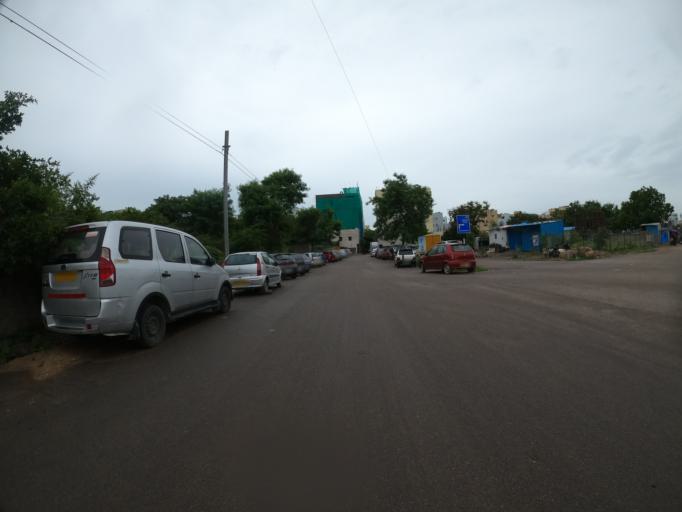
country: IN
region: Telangana
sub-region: Rangareddi
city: Kukatpalli
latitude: 17.4592
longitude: 78.3971
